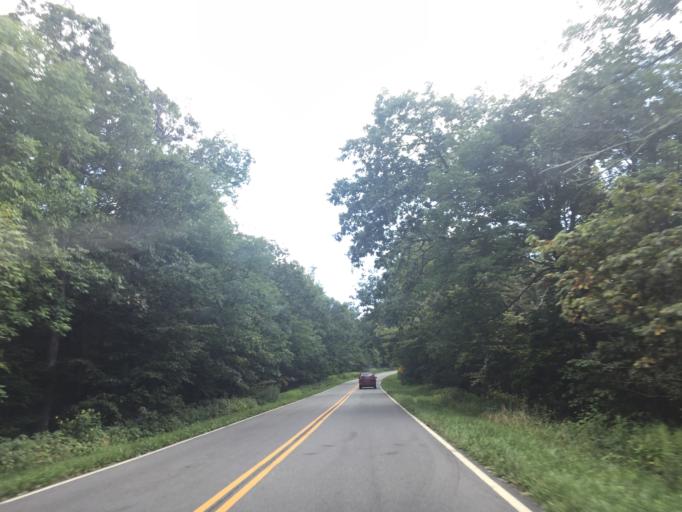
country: US
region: Virginia
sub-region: Rappahannock County
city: Washington
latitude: 38.7626
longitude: -78.2466
